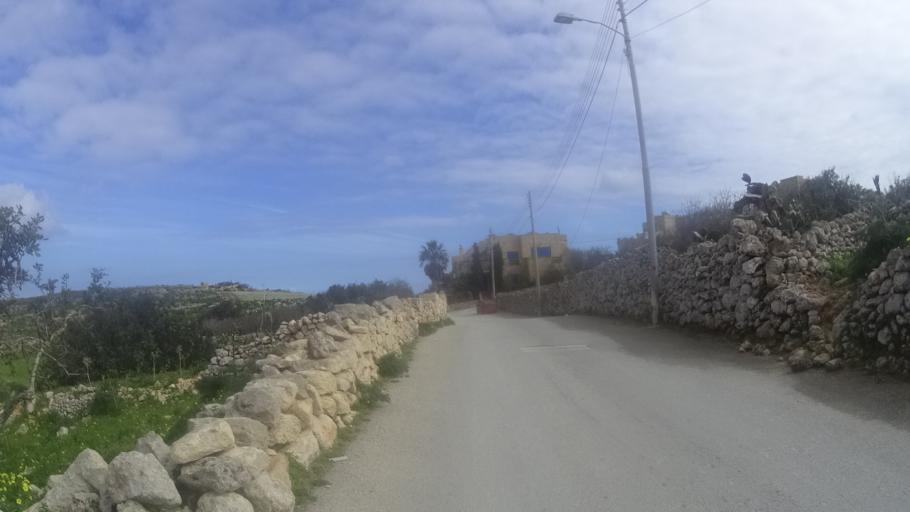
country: MT
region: Il-Qala
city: Qala
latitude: 36.0421
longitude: 14.3125
